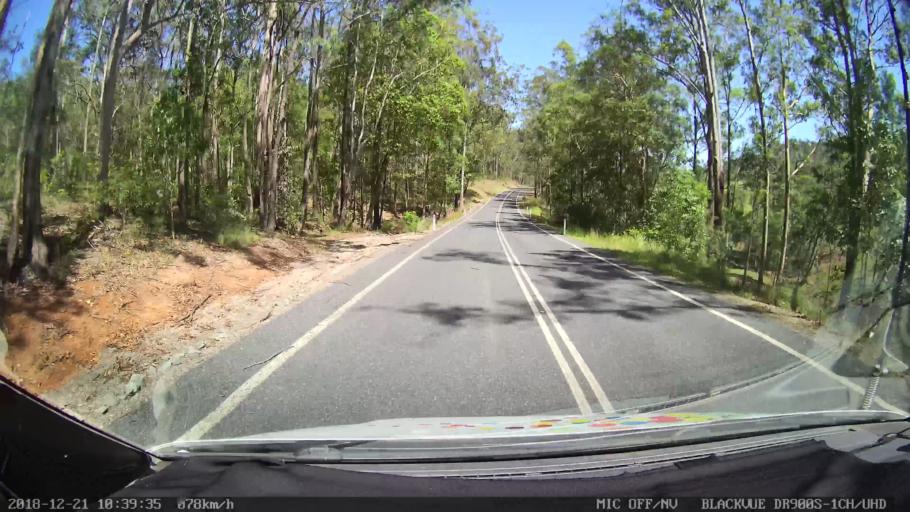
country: AU
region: New South Wales
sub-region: Clarence Valley
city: Gordon
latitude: -29.6069
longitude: 152.5950
